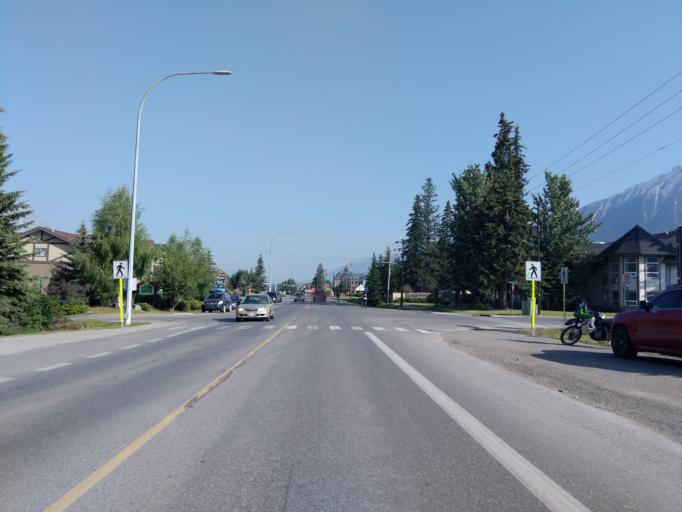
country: CA
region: Alberta
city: Canmore
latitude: 51.0857
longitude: -115.3453
